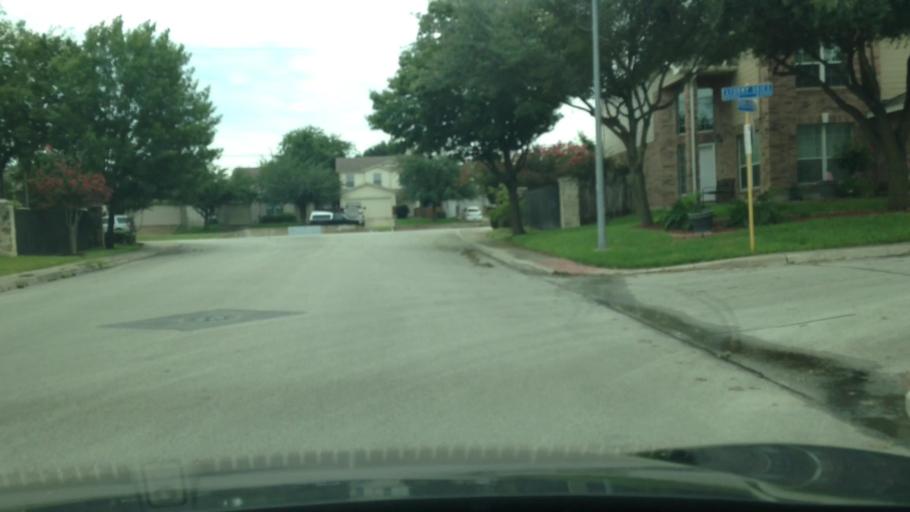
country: US
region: Texas
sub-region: Bexar County
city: Live Oak
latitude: 29.5850
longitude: -98.3830
